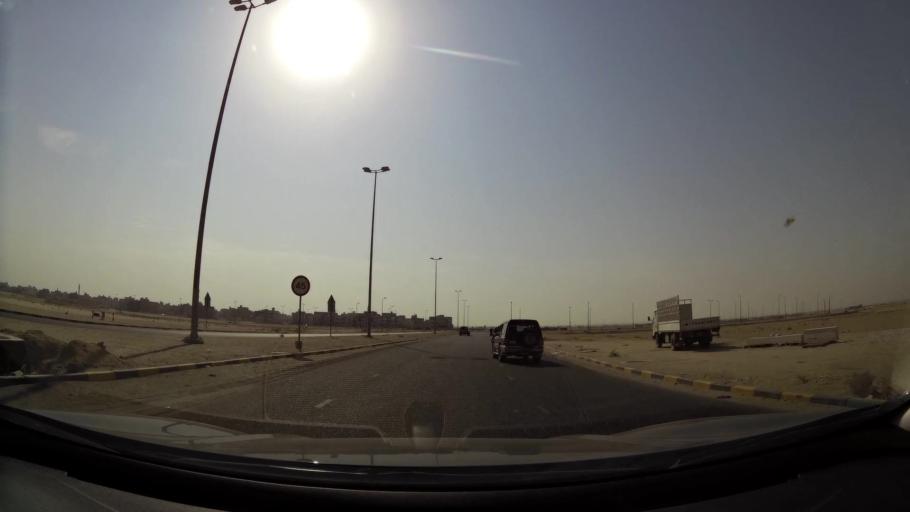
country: KW
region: Al Ahmadi
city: Al Wafrah
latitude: 28.7785
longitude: 48.0509
